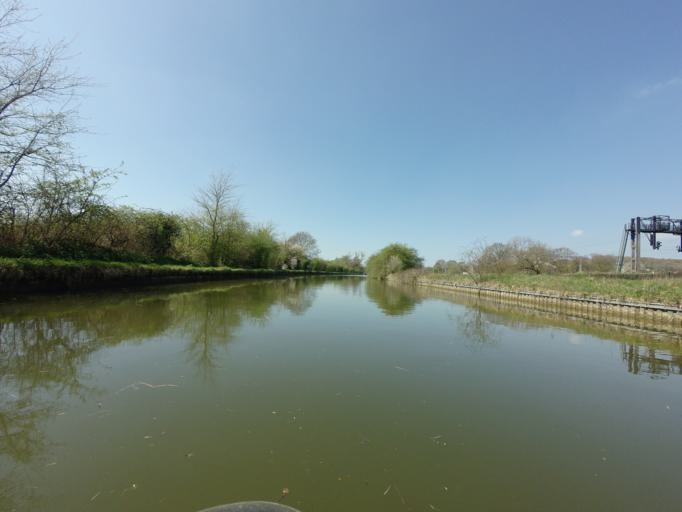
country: GB
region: England
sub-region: Hertfordshire
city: Berkhamsted
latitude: 51.7748
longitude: -0.5925
